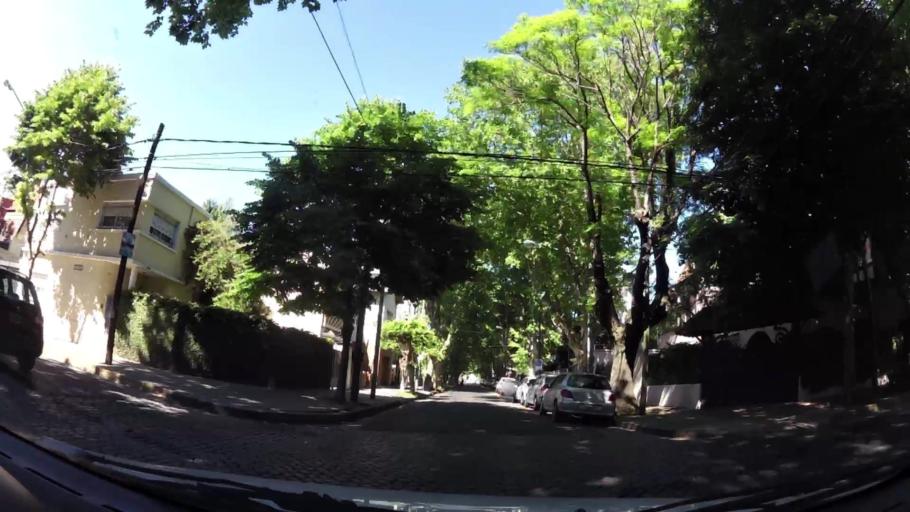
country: AR
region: Buenos Aires
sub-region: Partido de Vicente Lopez
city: Olivos
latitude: -34.5255
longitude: -58.4798
